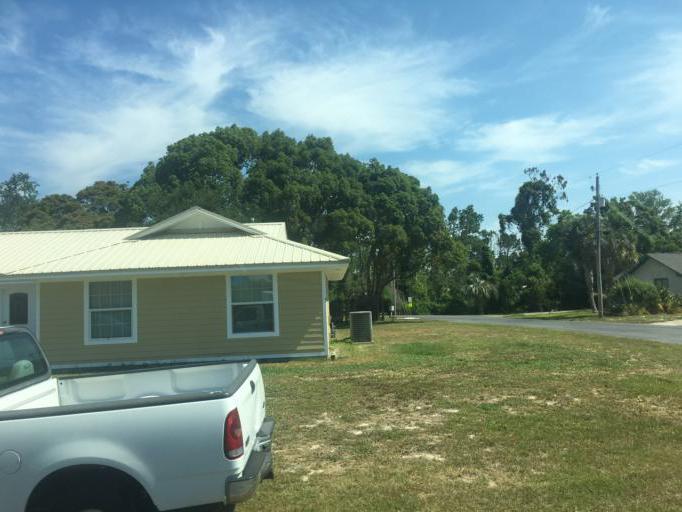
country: US
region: Florida
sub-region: Bay County
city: Upper Grand Lagoon
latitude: 30.1640
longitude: -85.7636
